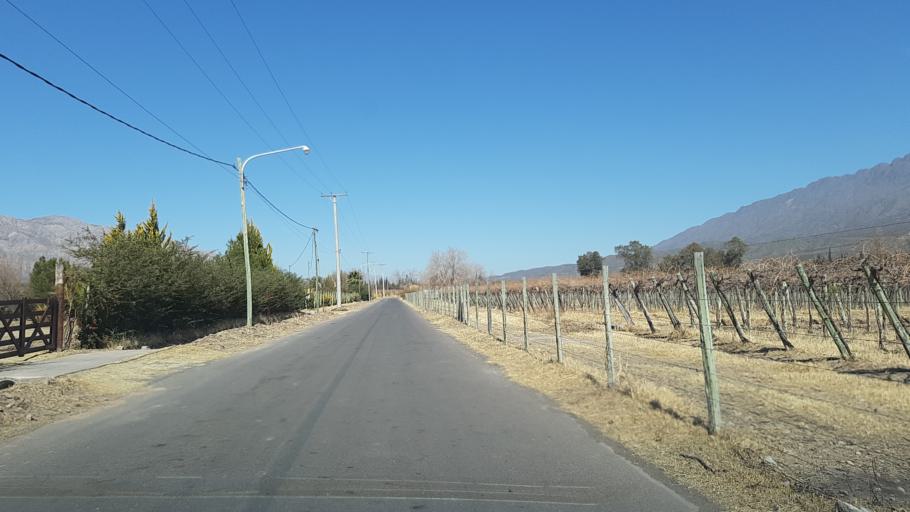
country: AR
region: San Juan
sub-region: Departamento de Zonda
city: Zonda
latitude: -31.5689
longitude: -68.7503
